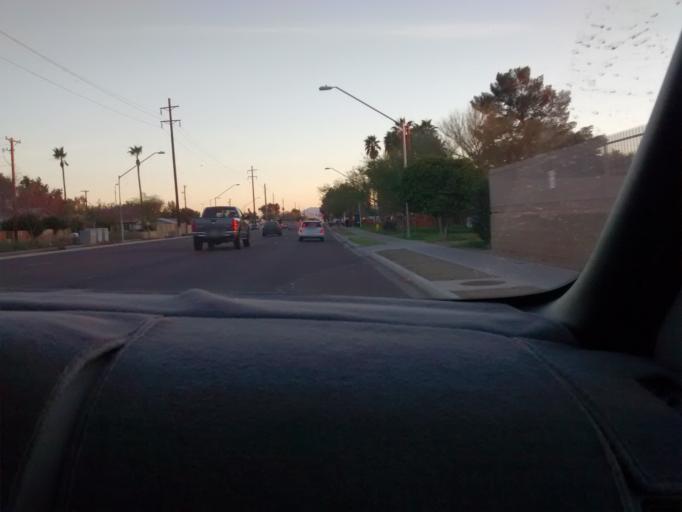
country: US
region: Arizona
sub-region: Maricopa County
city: Glendale
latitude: 33.5274
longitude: -112.2033
